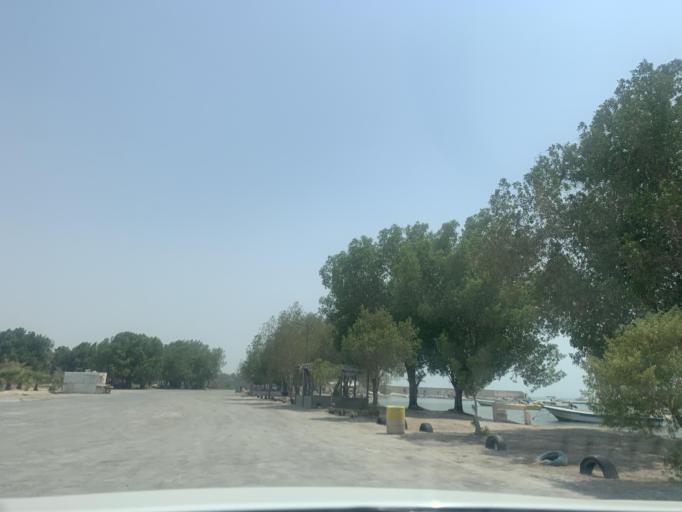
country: BH
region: Central Governorate
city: Madinat Hamad
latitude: 26.1238
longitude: 50.4614
